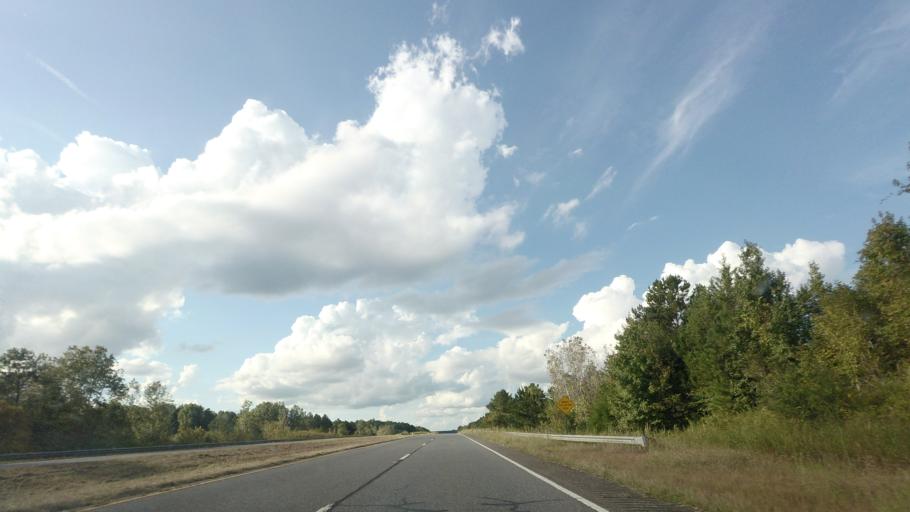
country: US
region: Georgia
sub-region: Houston County
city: Perry
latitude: 32.4011
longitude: -83.6432
